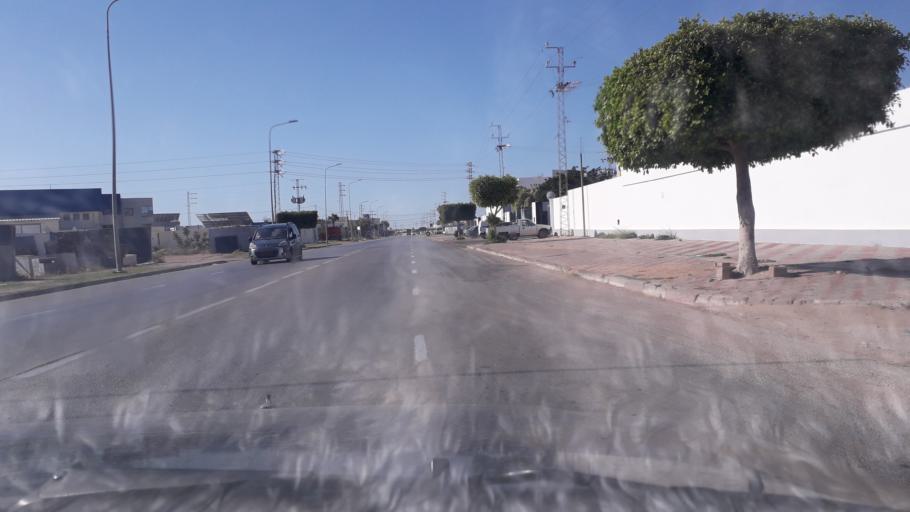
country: TN
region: Safaqis
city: Al Qarmadah
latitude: 34.8498
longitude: 10.7615
